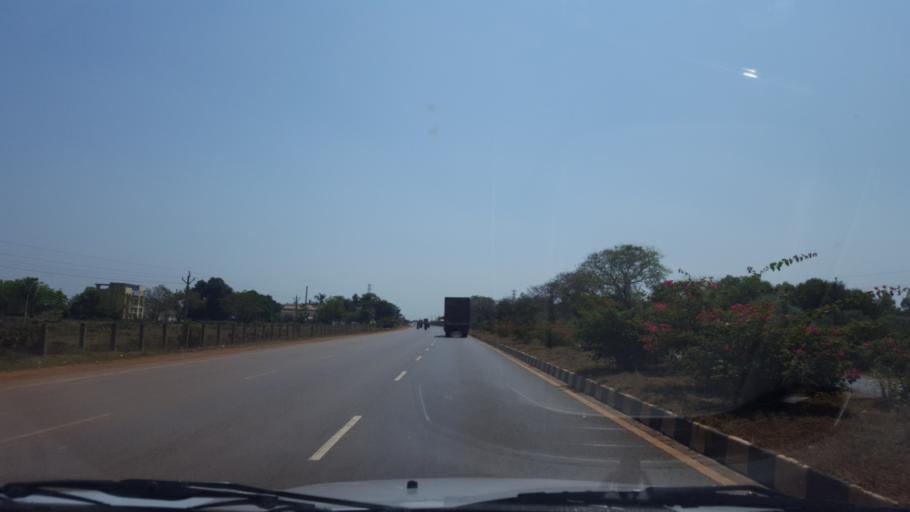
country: IN
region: Andhra Pradesh
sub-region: Nellore
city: Kavali
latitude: 14.8058
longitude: 79.9963
